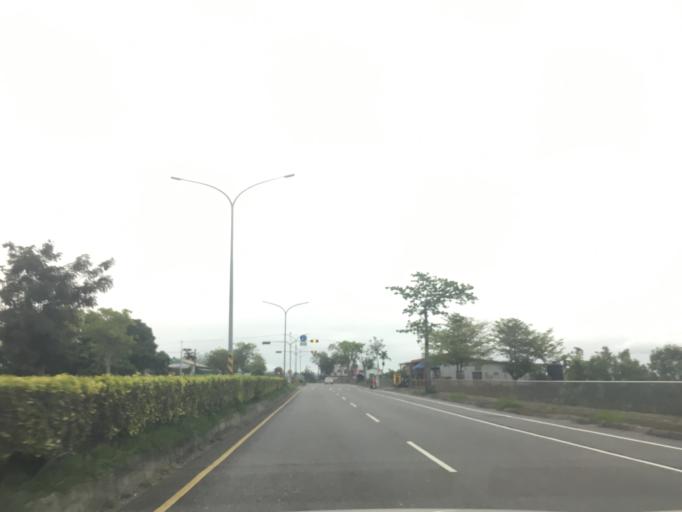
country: TW
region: Taiwan
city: Taitung City
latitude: 22.7165
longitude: 121.0498
